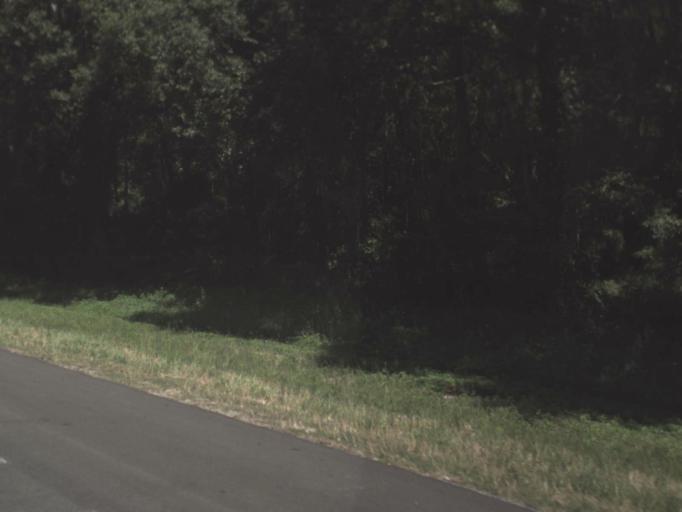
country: US
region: Florida
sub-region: Madison County
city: Madison
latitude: 30.4100
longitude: -83.4165
